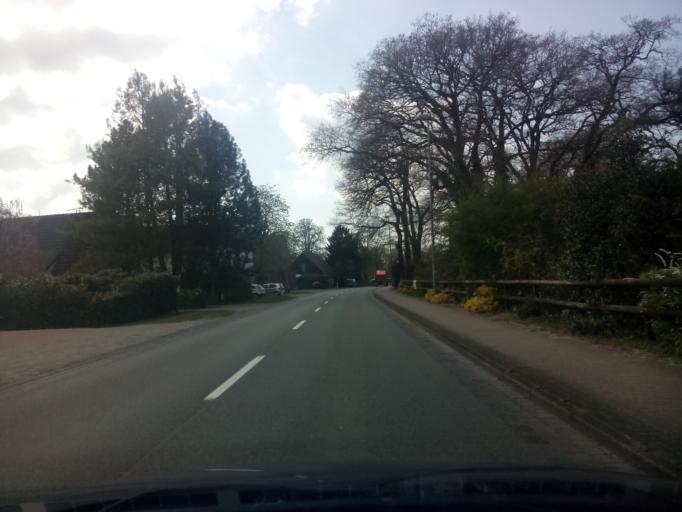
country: DE
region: Lower Saxony
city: Lilienthal
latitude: 53.1726
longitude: 8.9108
